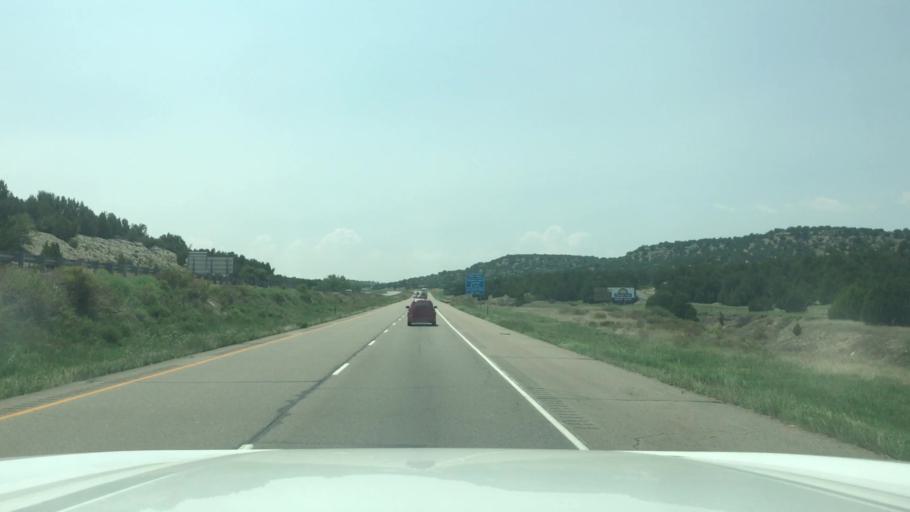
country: US
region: Colorado
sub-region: Pueblo County
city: Colorado City
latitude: 37.9883
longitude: -104.7697
